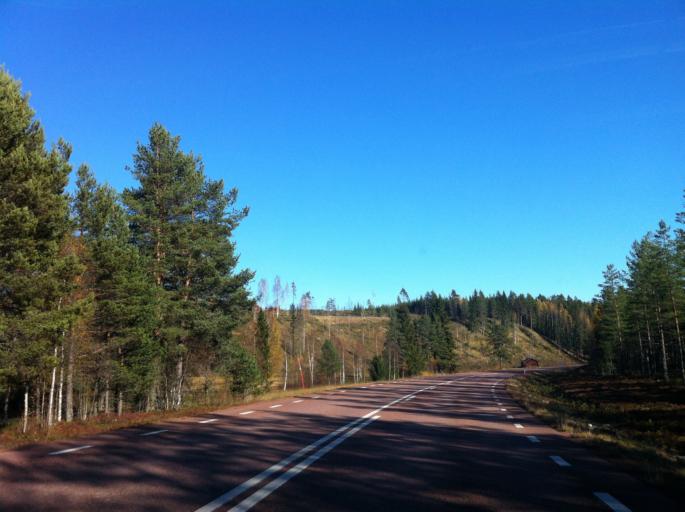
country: SE
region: Dalarna
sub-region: Alvdalens Kommun
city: AElvdalen
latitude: 61.2787
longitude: 13.9333
